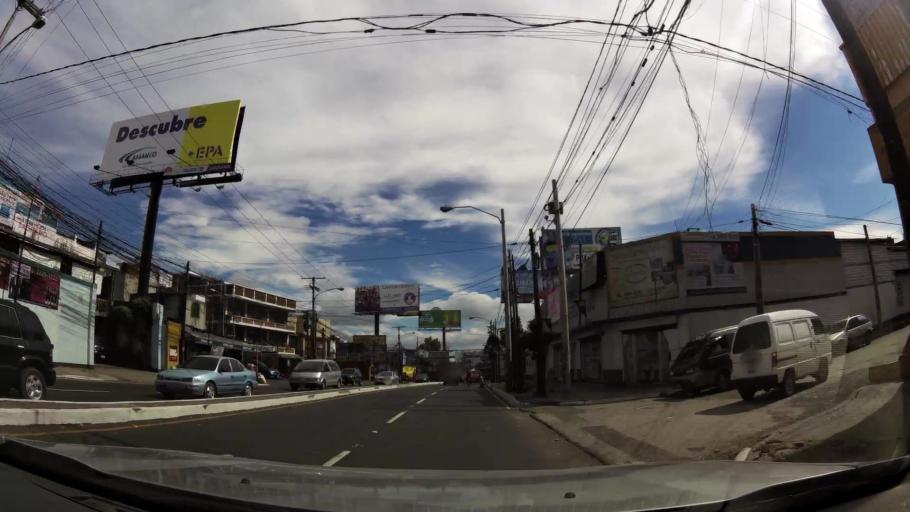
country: GT
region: Guatemala
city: Mixco
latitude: 14.6393
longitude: -90.5652
